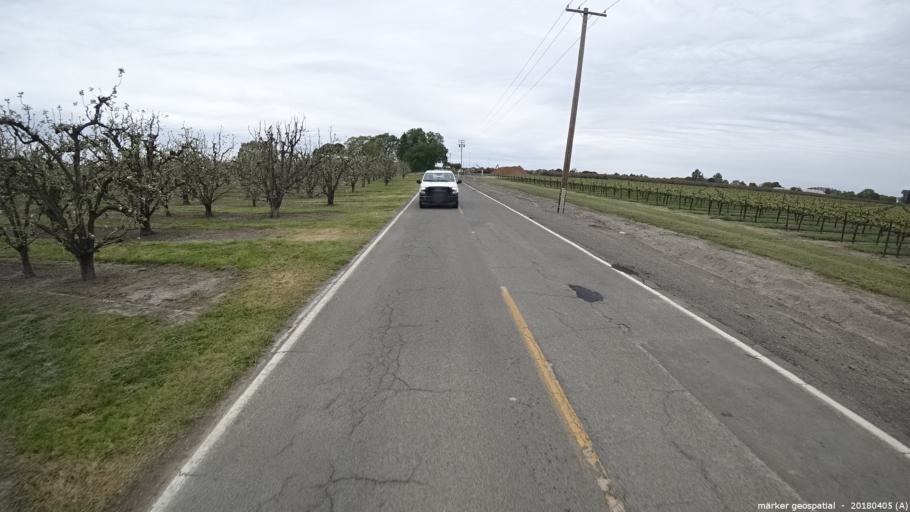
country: US
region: California
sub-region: Sacramento County
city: Walnut Grove
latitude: 38.3383
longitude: -121.5390
